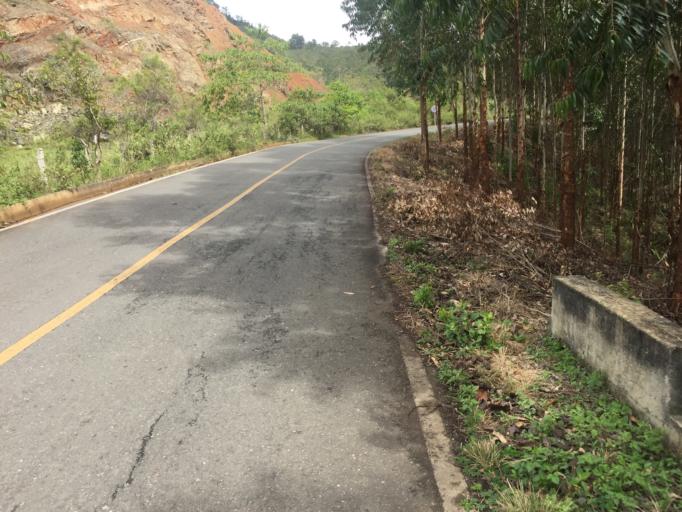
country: CO
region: Valle del Cauca
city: Dagua
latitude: 3.7025
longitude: -76.5873
